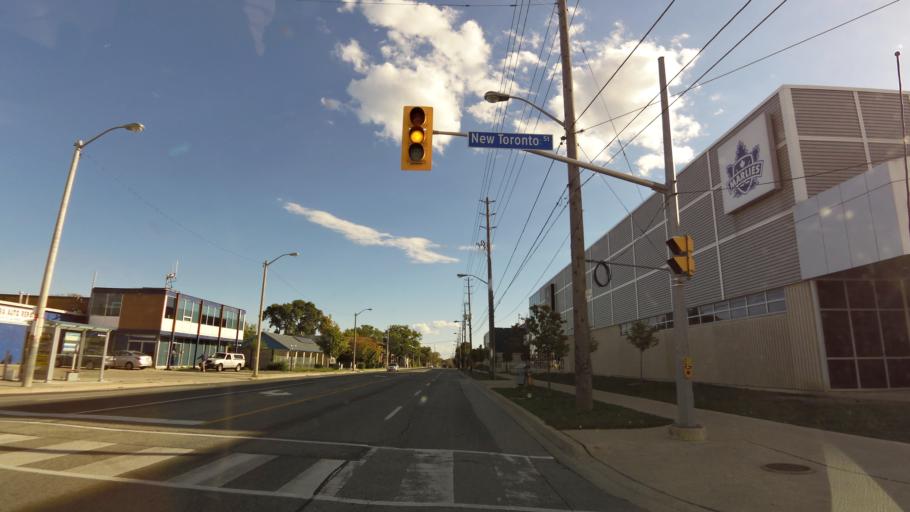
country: CA
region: Ontario
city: Etobicoke
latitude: 43.6040
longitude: -79.5194
